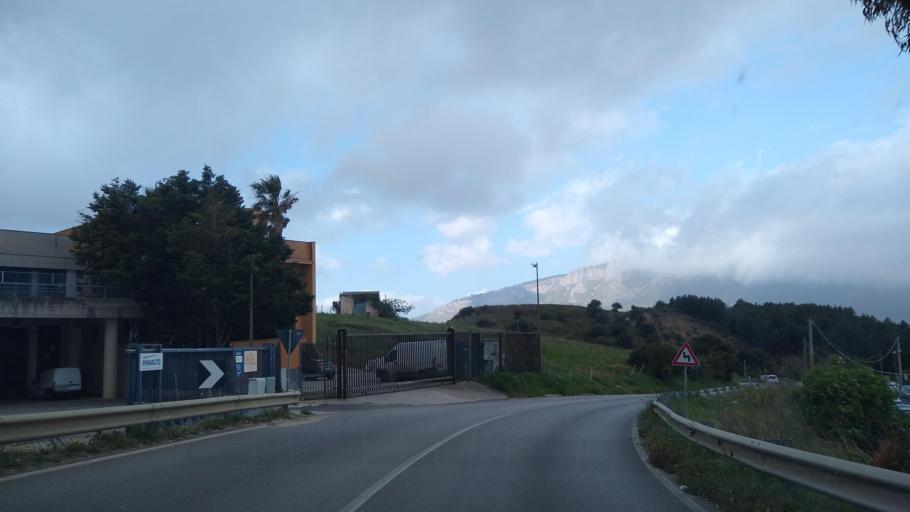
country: IT
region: Sicily
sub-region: Trapani
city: Alcamo
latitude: 37.9762
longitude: 12.9422
